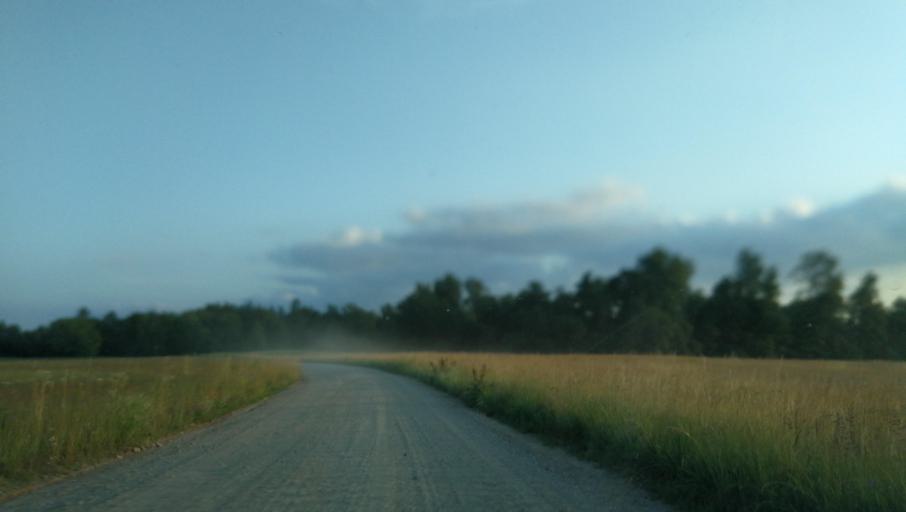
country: LV
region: Cesu Rajons
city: Cesis
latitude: 57.2838
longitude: 25.2431
